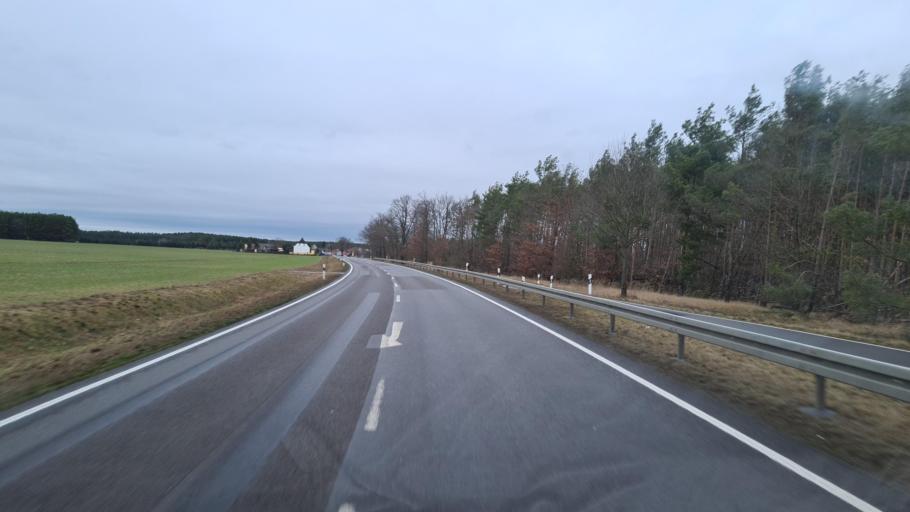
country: DE
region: Brandenburg
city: Bad Liebenwerda
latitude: 51.5429
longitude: 13.3932
